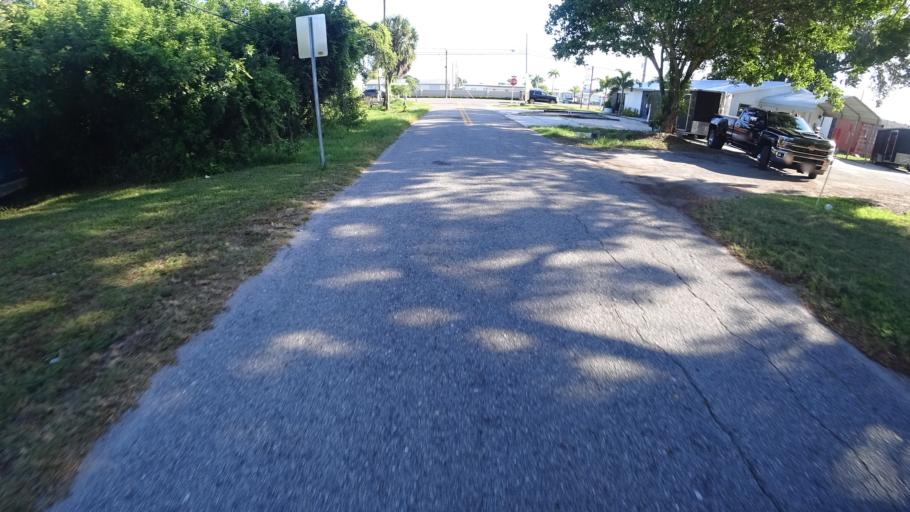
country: US
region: Florida
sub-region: Manatee County
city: South Bradenton
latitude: 27.4473
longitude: -82.5708
